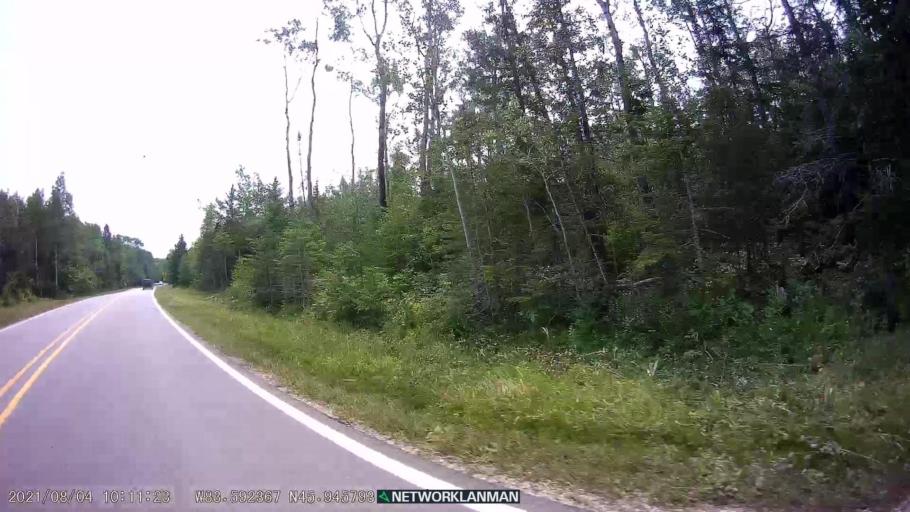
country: CA
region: Ontario
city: Thessalon
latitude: 45.9457
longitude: -83.5920
